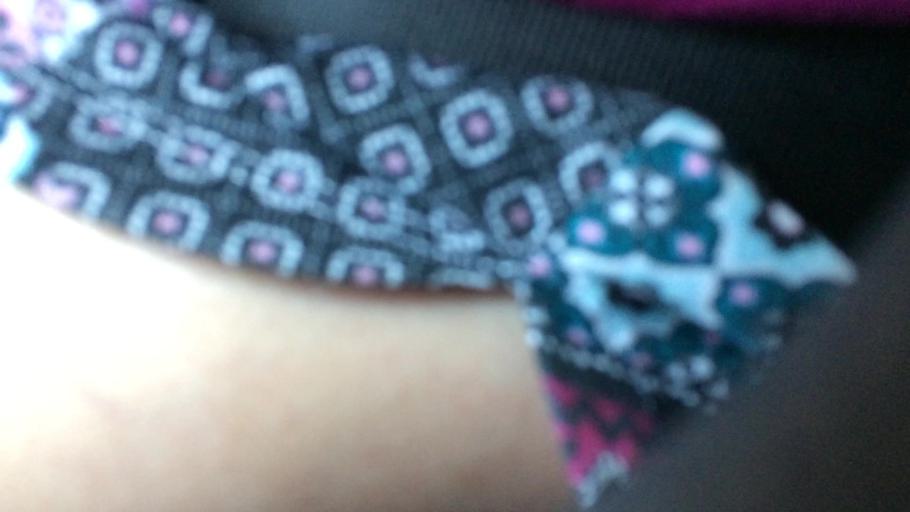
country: US
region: New Mexico
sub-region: Colfax County
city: Springer
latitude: 35.9606
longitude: -104.7634
